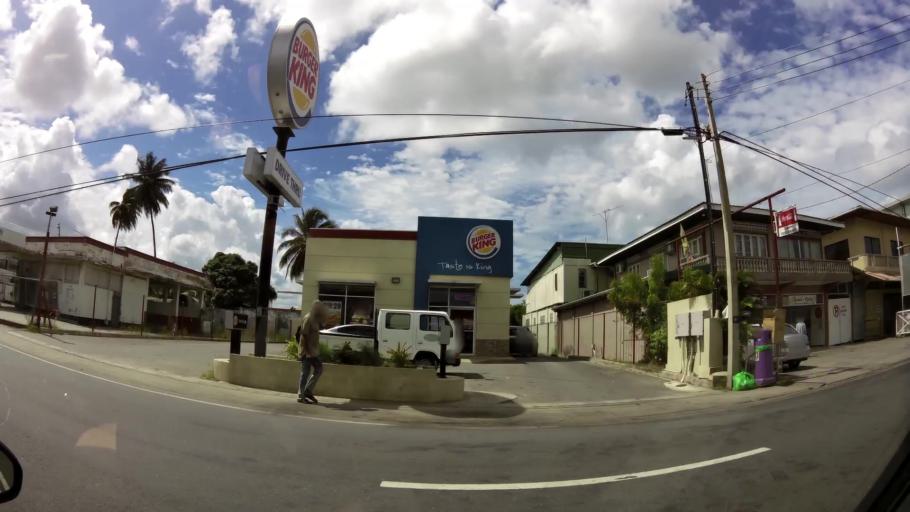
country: TT
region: City of San Fernando
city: Marabella
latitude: 10.3048
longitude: -61.4509
